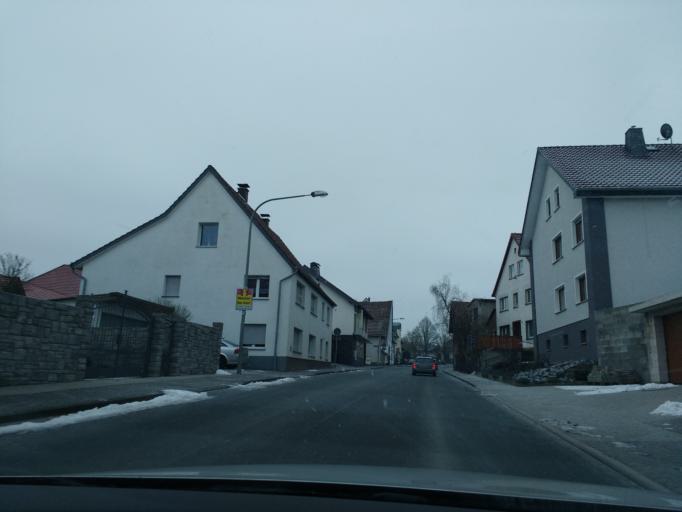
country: DE
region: North Rhine-Westphalia
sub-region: Regierungsbezirk Detmold
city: Wunnenberg
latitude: 51.5183
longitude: 8.6978
